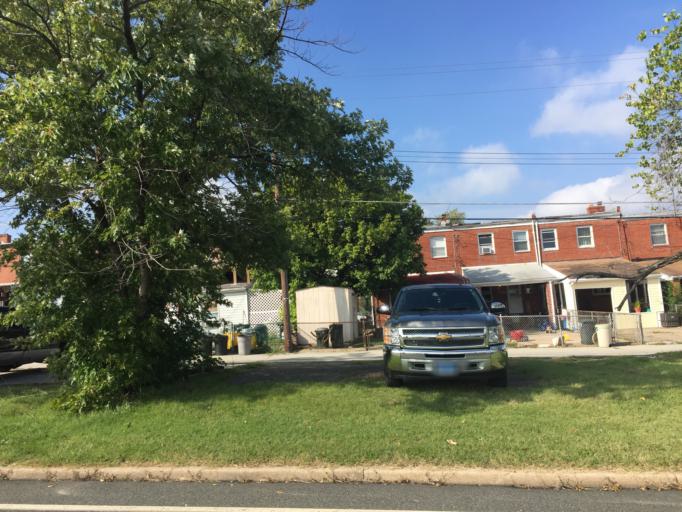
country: US
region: Maryland
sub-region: Baltimore County
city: Dundalk
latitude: 39.2816
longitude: -76.5058
